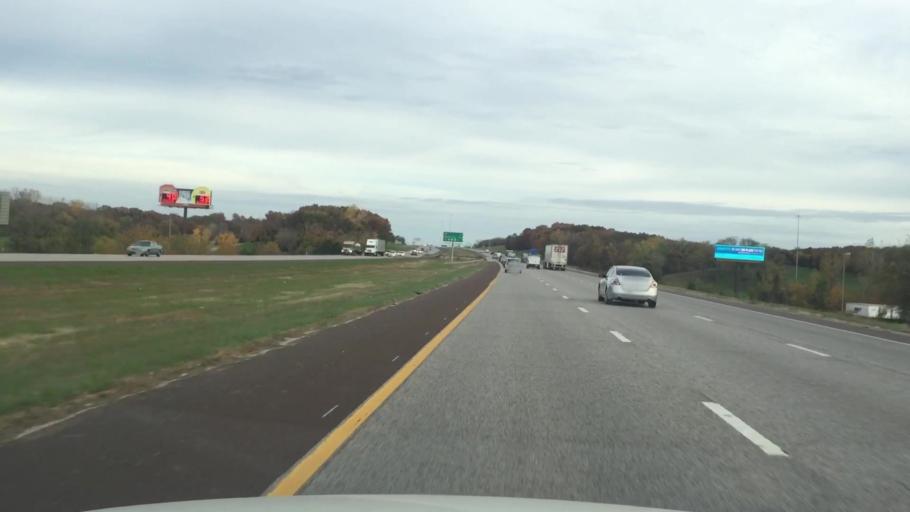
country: US
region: Kansas
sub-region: Wyandotte County
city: Edwardsville
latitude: 39.0591
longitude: -94.7913
